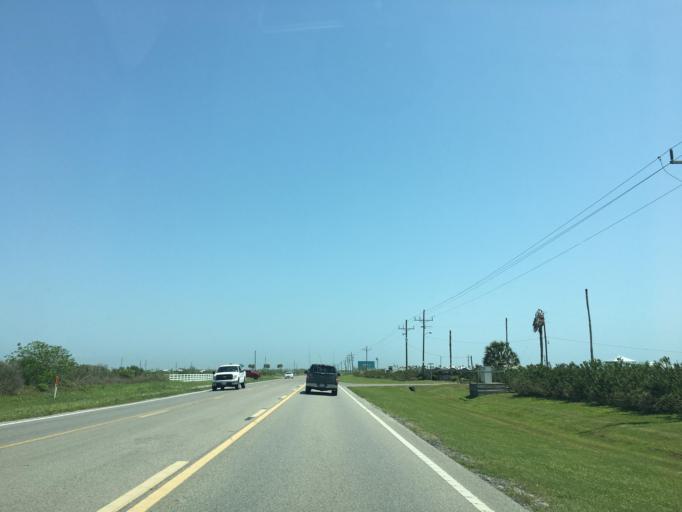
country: US
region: Texas
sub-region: Galveston County
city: Bolivar Peninsula
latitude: 29.4348
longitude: -94.6790
